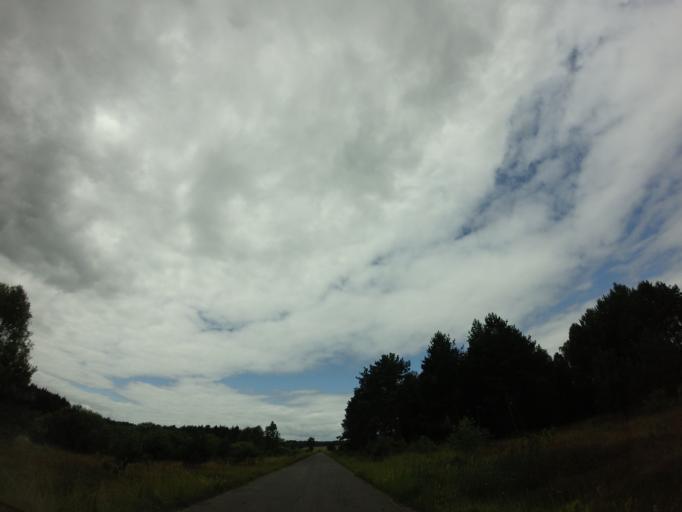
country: PL
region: West Pomeranian Voivodeship
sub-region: Powiat stargardzki
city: Insko
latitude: 53.3657
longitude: 15.5989
